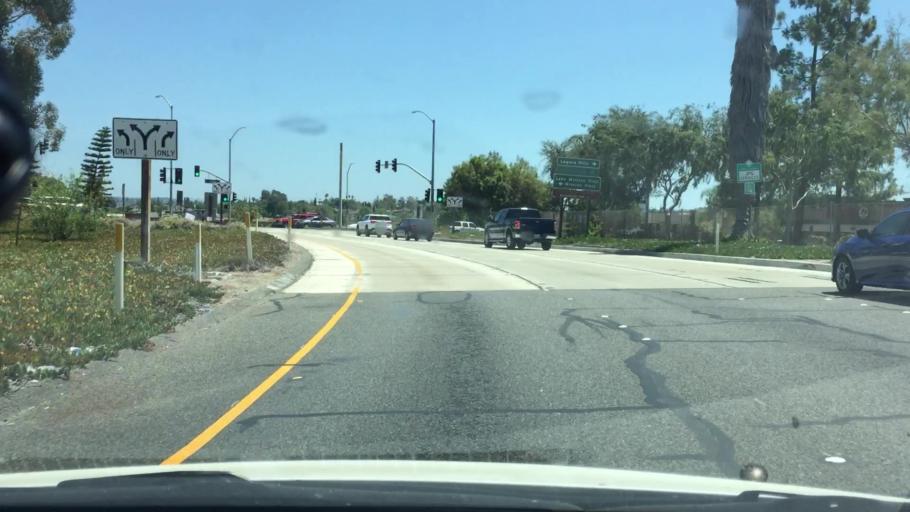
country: US
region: California
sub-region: Orange County
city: Mission Viejo
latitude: 33.6037
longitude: -117.6917
